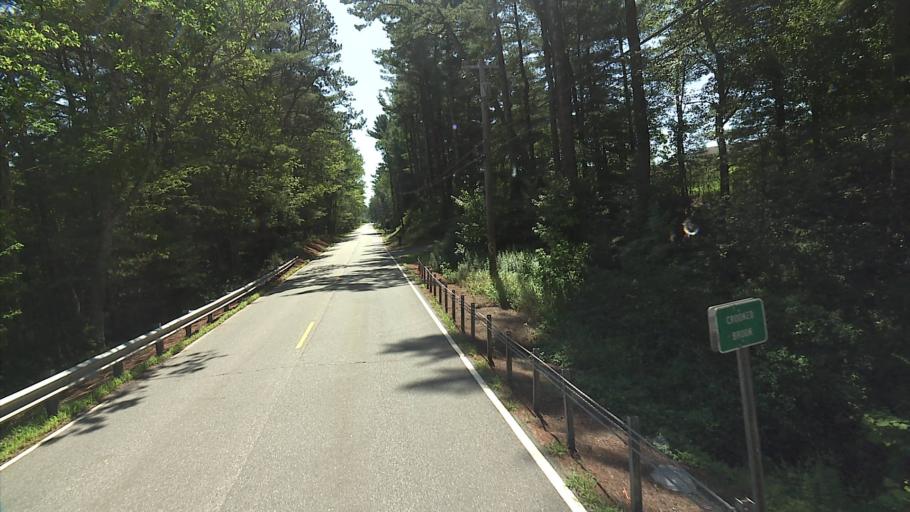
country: US
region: Connecticut
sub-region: Windham County
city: Moosup
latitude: 41.7005
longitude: -71.7994
